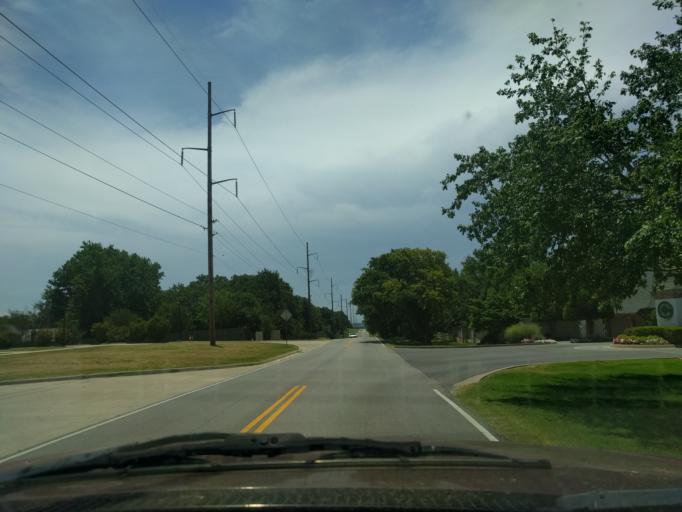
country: US
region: Oklahoma
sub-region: Tulsa County
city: Jenks
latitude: 36.0017
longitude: -95.9223
